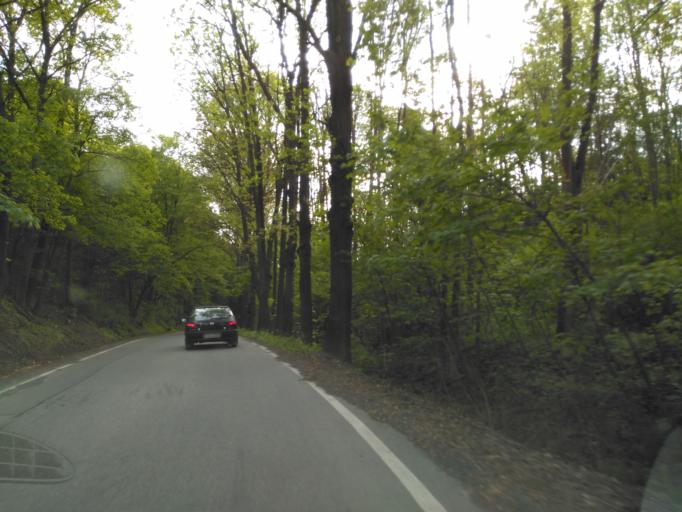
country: CZ
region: Central Bohemia
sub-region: Okres Beroun
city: Kraluv Dvur
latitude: 49.9193
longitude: 14.0436
